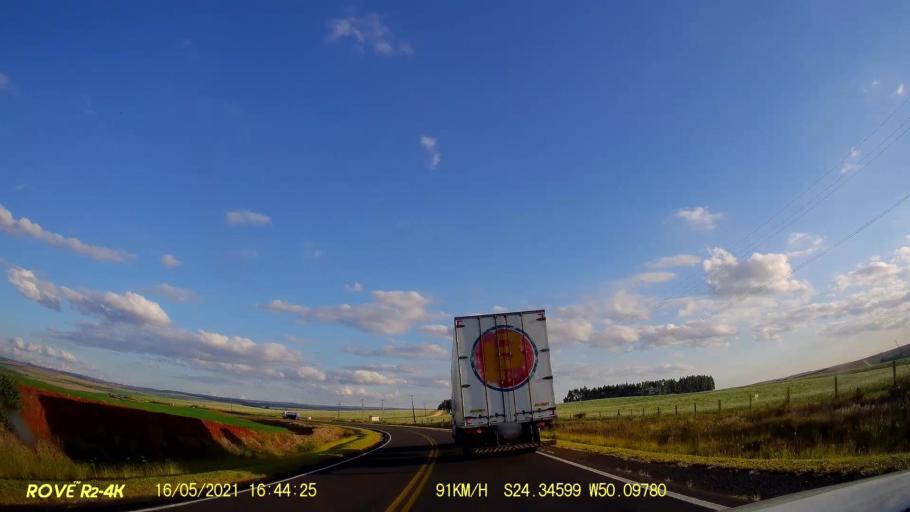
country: BR
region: Parana
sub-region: Pirai Do Sul
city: Pirai do Sul
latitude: -24.3458
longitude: -50.0977
